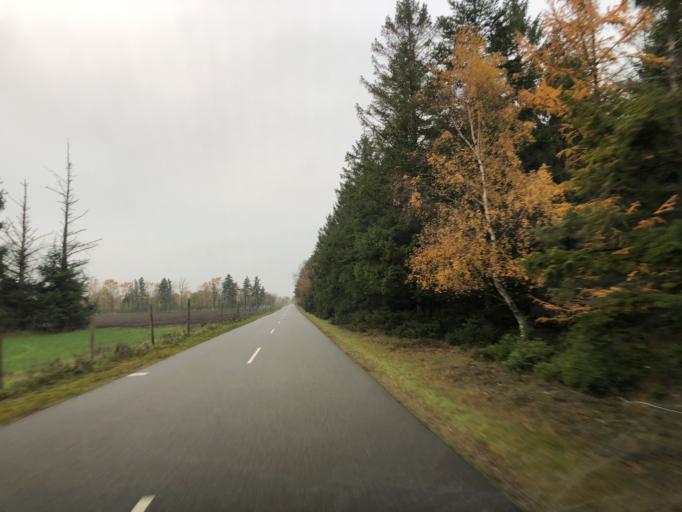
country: DK
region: Central Jutland
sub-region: Herning Kommune
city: Snejbjerg
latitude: 56.2254
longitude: 8.9199
